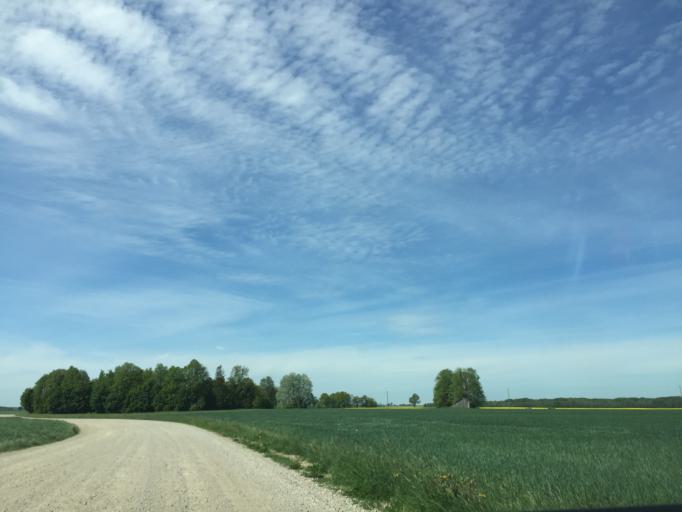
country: LT
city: Linkuva
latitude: 56.0971
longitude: 24.1279
